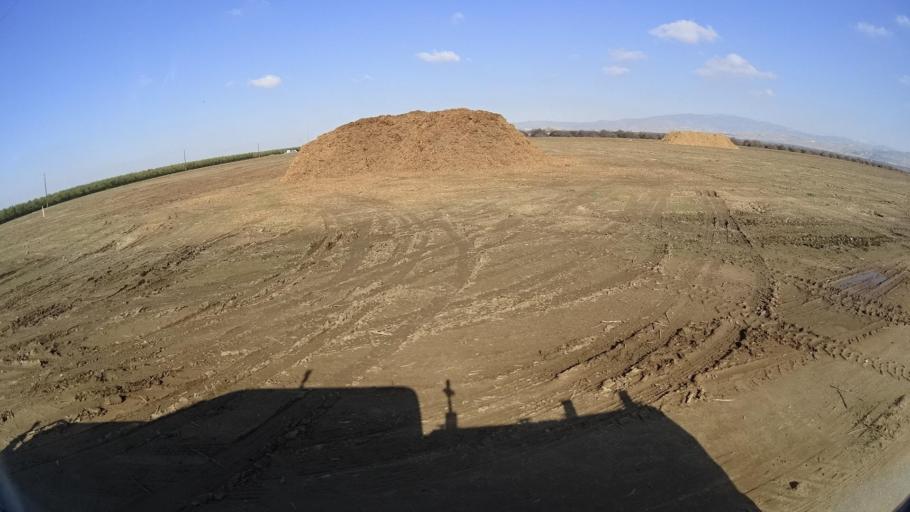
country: US
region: California
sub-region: Kern County
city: Arvin
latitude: 35.2235
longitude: -118.7958
